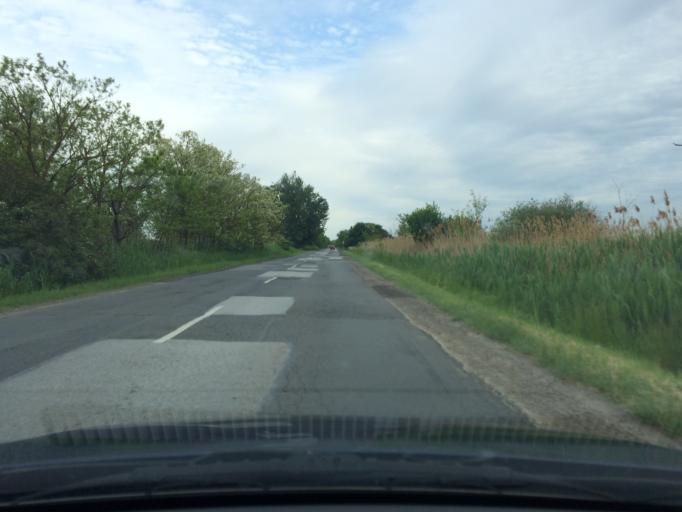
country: HU
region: Hajdu-Bihar
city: Hajdunanas
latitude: 47.8949
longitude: 21.4101
